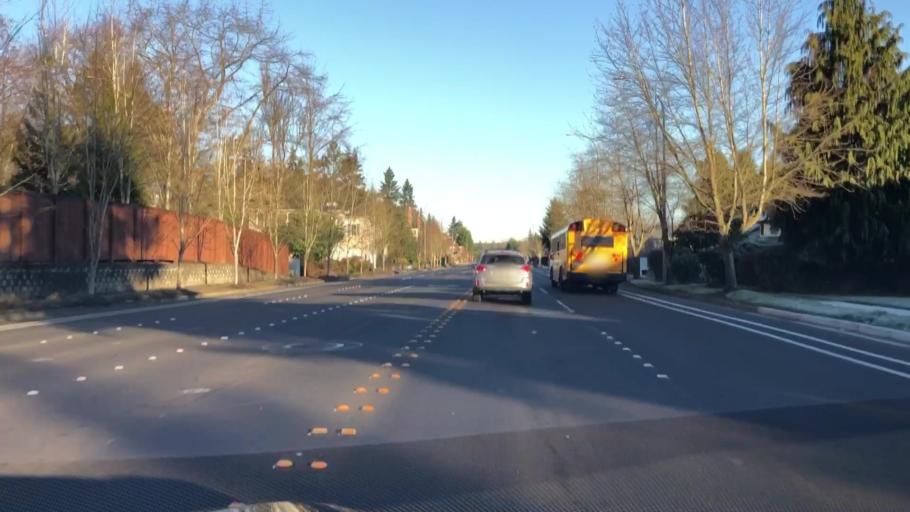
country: US
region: Washington
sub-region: King County
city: Newport
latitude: 47.5877
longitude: -122.1643
